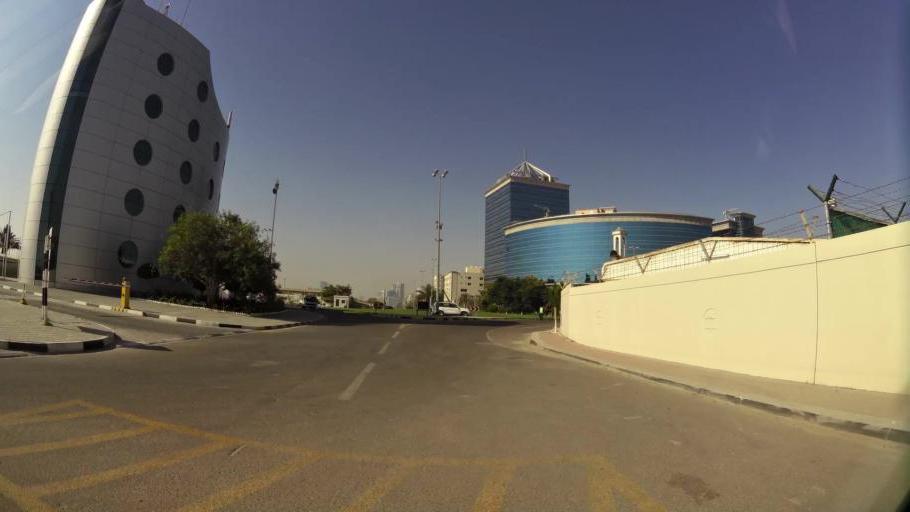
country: AE
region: Ajman
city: Ajman
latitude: 25.4205
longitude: 55.4537
